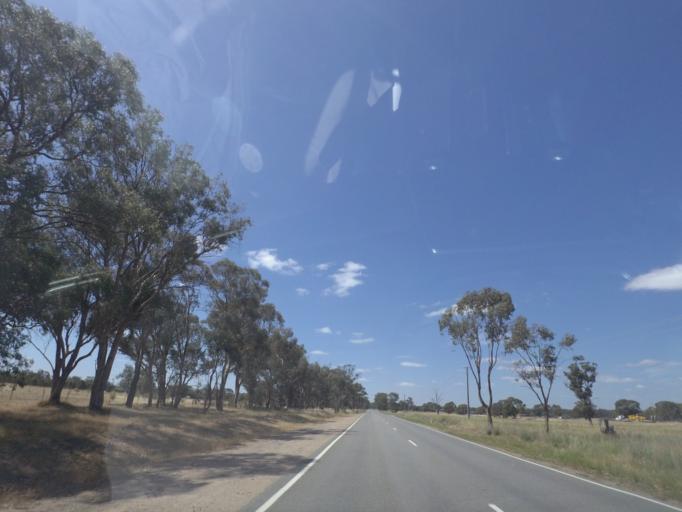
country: AU
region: Victoria
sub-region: Wangaratta
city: Wangaratta
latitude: -36.4186
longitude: 146.2630
